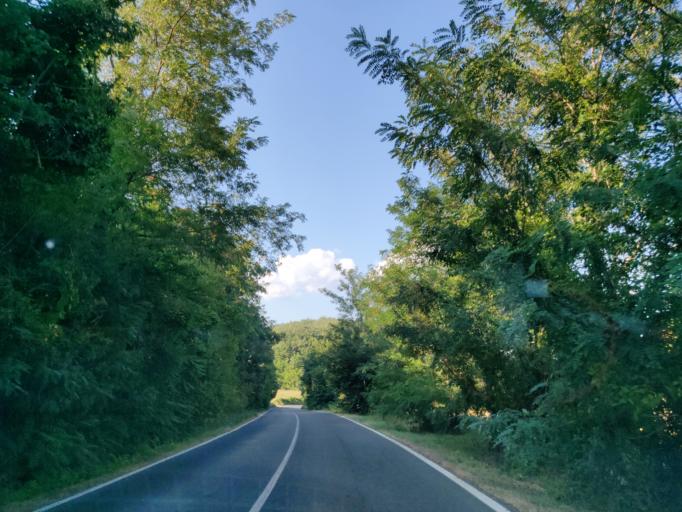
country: IT
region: Latium
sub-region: Provincia di Viterbo
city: Gradoli
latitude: 42.6510
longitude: 11.8430
